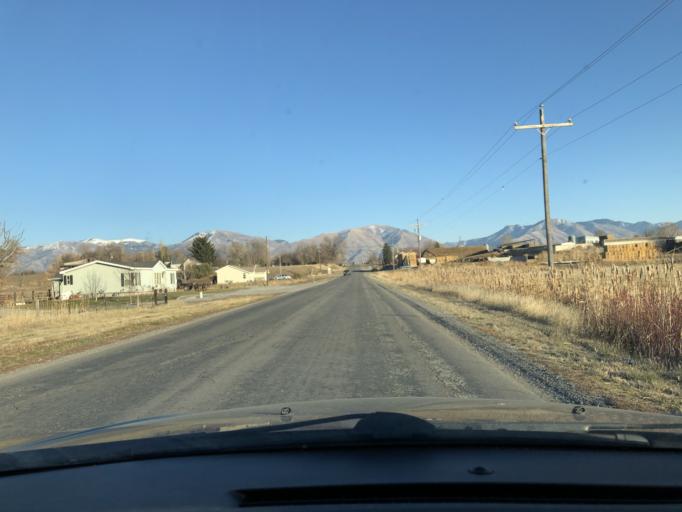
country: US
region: Utah
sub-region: Cache County
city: Wellsville
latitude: 41.6472
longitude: -111.9183
